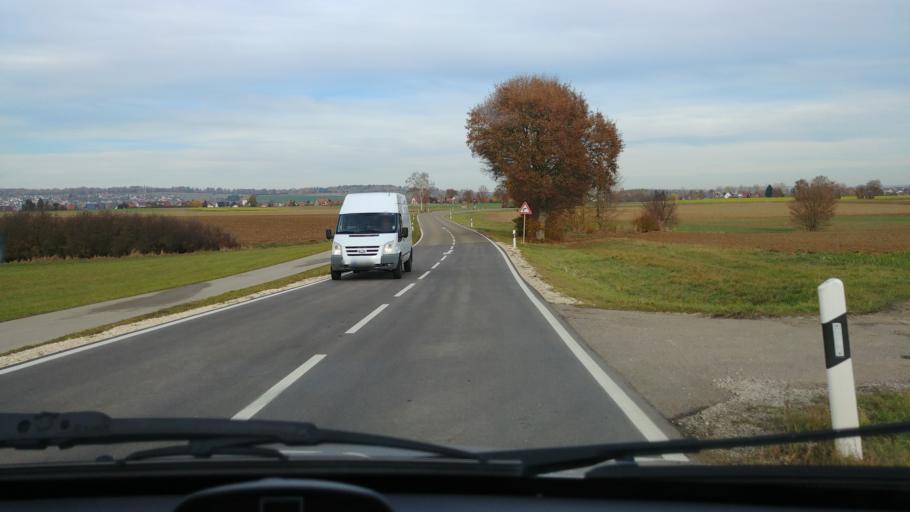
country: DE
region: Bavaria
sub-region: Swabia
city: Bachhagel
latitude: 48.6322
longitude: 10.3006
